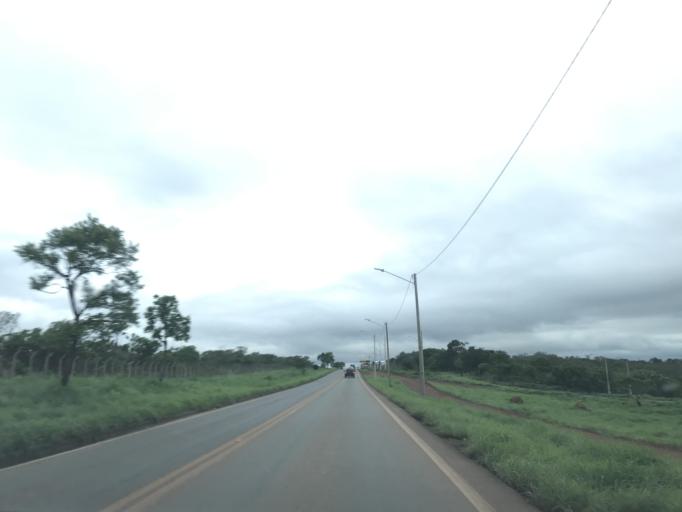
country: BR
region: Goias
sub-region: Luziania
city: Luziania
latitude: -16.2631
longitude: -47.9695
